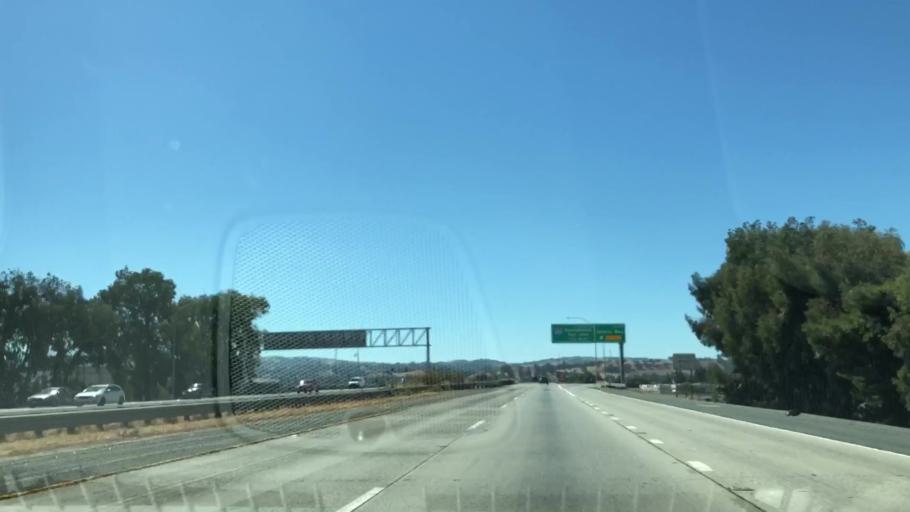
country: US
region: California
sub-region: Contra Costa County
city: Concord
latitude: 38.0030
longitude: -122.0459
